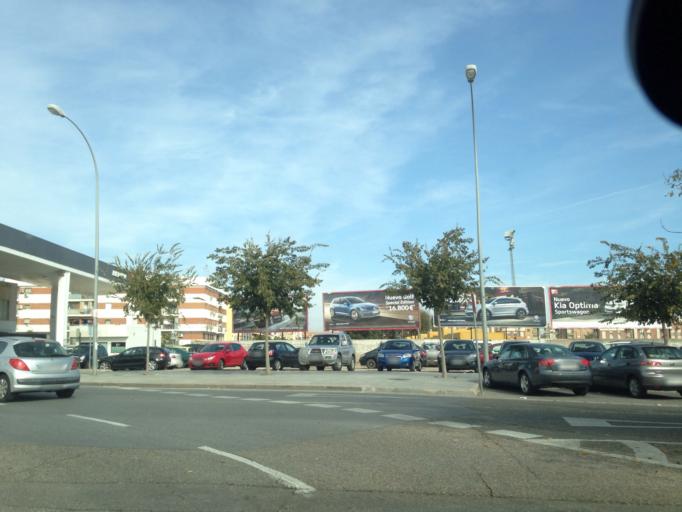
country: ES
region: Andalusia
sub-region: Province of Cordoba
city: Cordoba
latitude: 37.8764
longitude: -4.7664
